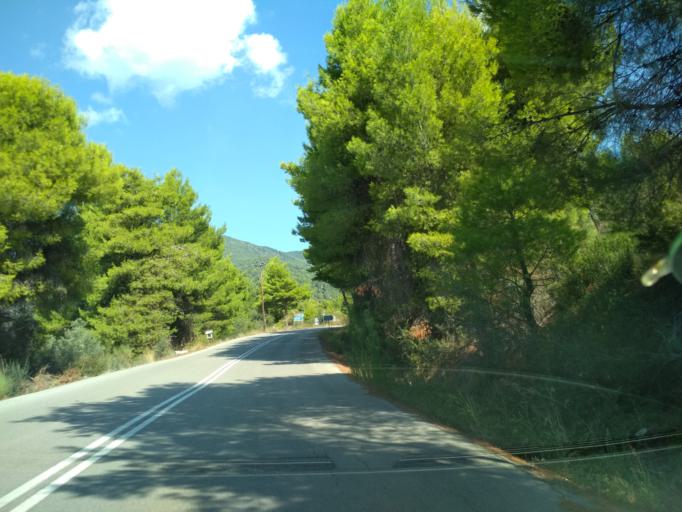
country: GR
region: Central Greece
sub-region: Nomos Evvoias
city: Roviai
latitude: 38.8225
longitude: 23.2291
